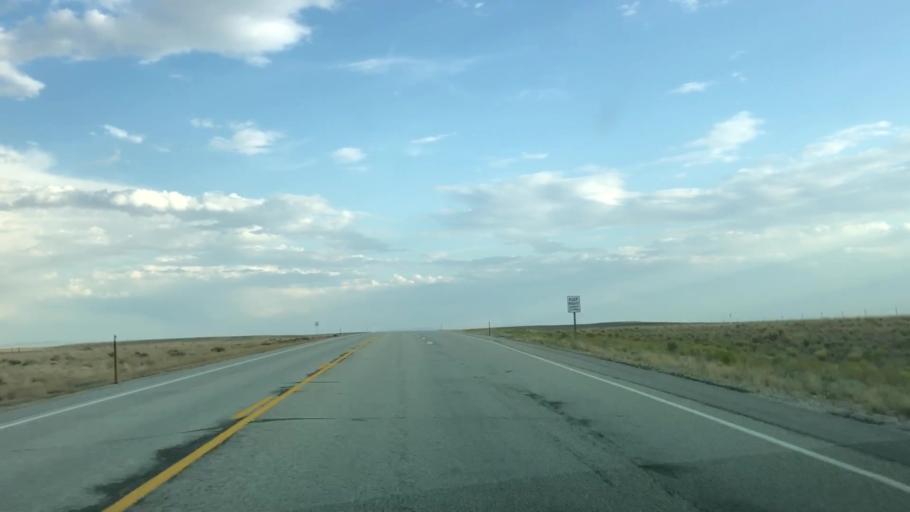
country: US
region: Wyoming
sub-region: Sweetwater County
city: North Rock Springs
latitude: 42.2767
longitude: -109.4831
